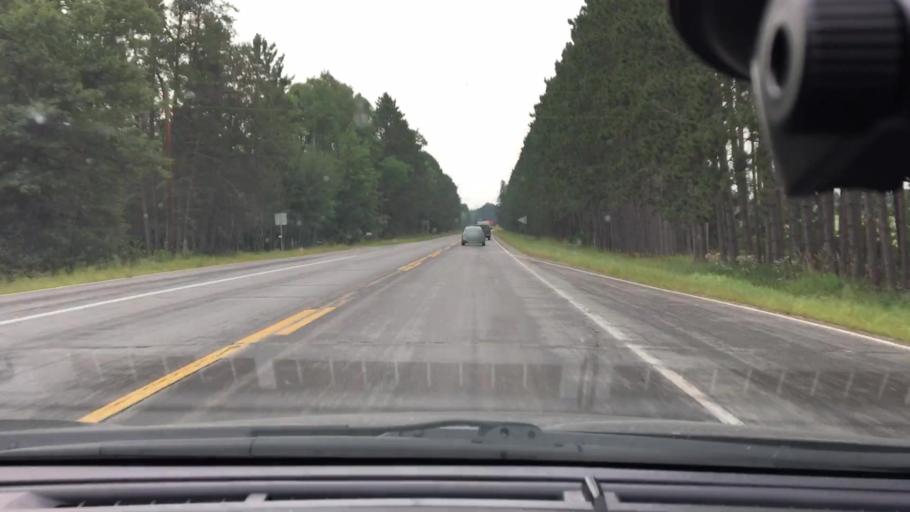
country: US
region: Minnesota
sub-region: Crow Wing County
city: Cross Lake
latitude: 46.7595
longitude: -93.9666
